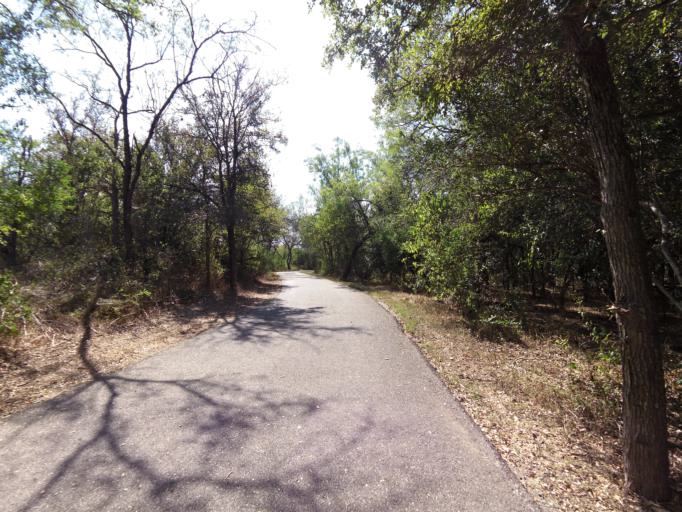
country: US
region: Texas
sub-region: Bexar County
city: China Grove
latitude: 29.3887
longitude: -98.4231
